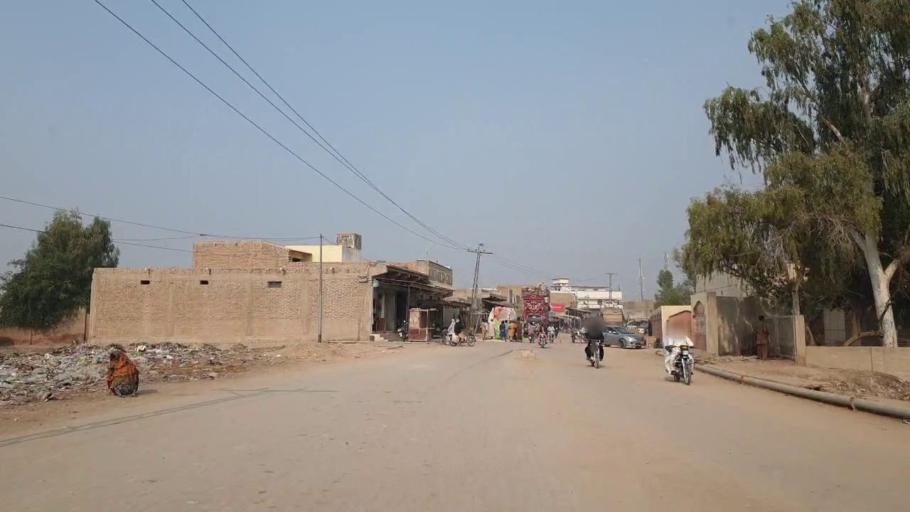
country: PK
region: Sindh
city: Bhan
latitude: 26.5539
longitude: 67.7186
